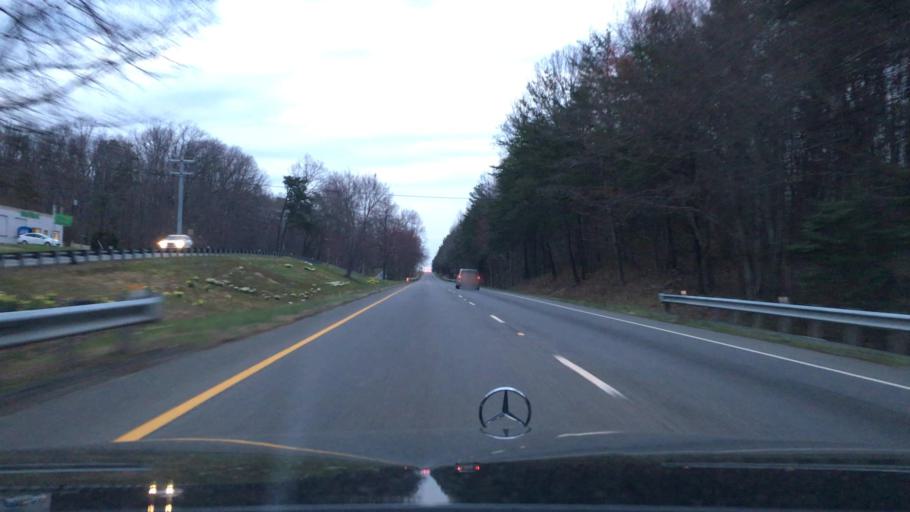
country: US
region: Virginia
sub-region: Albemarle County
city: Hollymead
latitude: 38.1754
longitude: -78.4072
